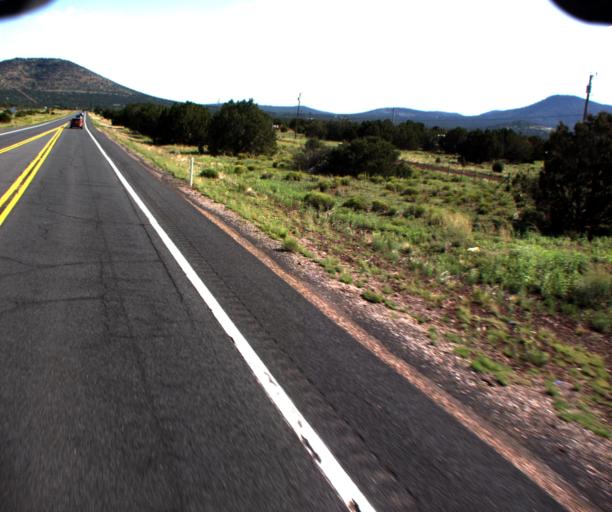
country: US
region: Arizona
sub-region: Coconino County
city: Williams
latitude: 35.3690
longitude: -112.1644
